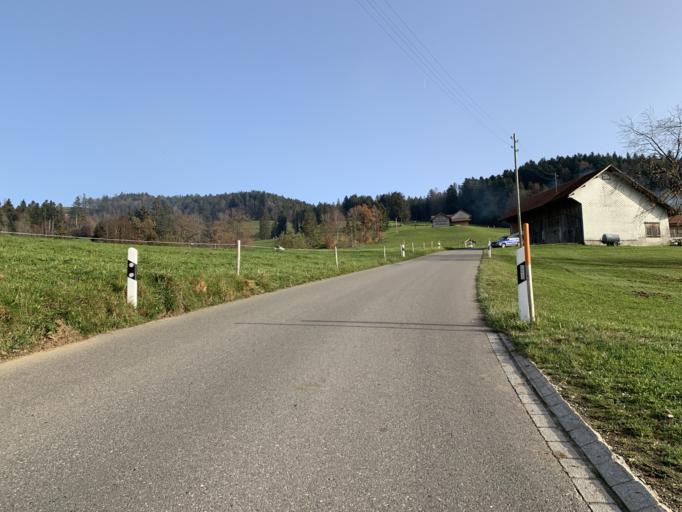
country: CH
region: Zurich
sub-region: Bezirk Hinwil
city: Hadlikon
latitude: 47.3051
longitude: 8.8749
